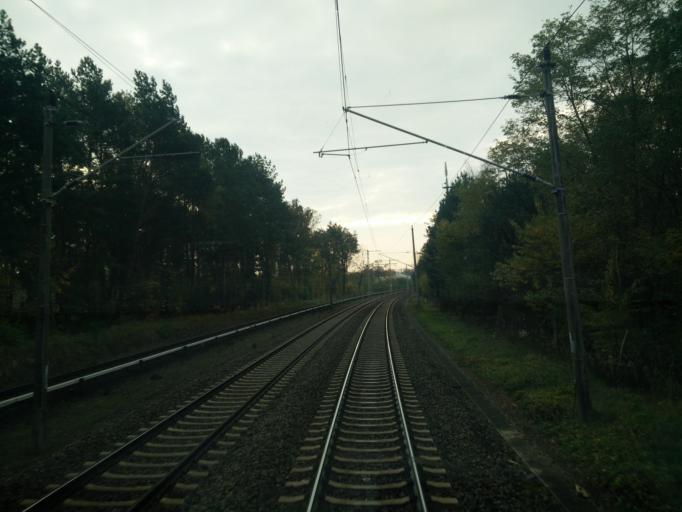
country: DE
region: Brandenburg
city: Wildau
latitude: 52.3341
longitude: 13.6367
